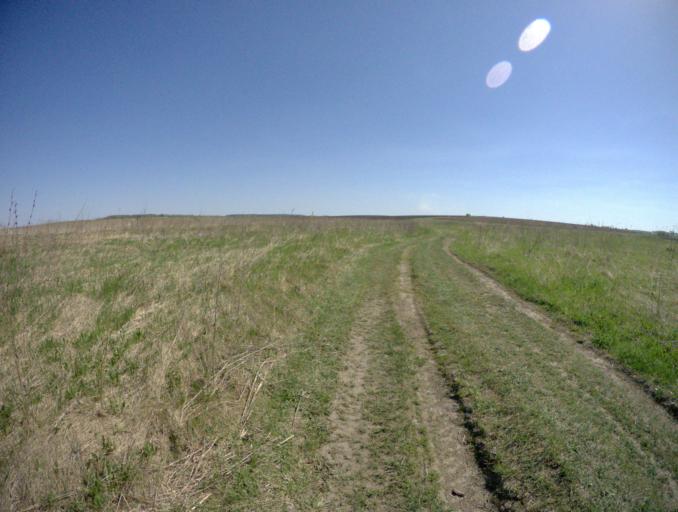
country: RU
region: Vladimir
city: Vladimir
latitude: 56.2783
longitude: 40.3392
